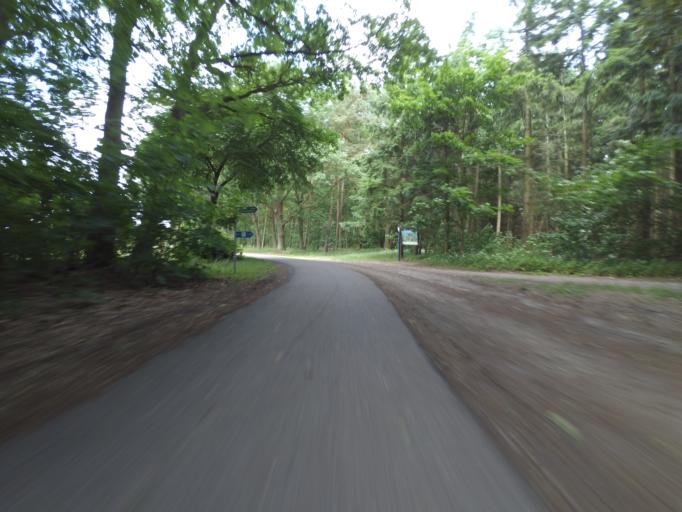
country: DE
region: Mecklenburg-Vorpommern
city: Malchow
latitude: 53.4878
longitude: 12.5074
